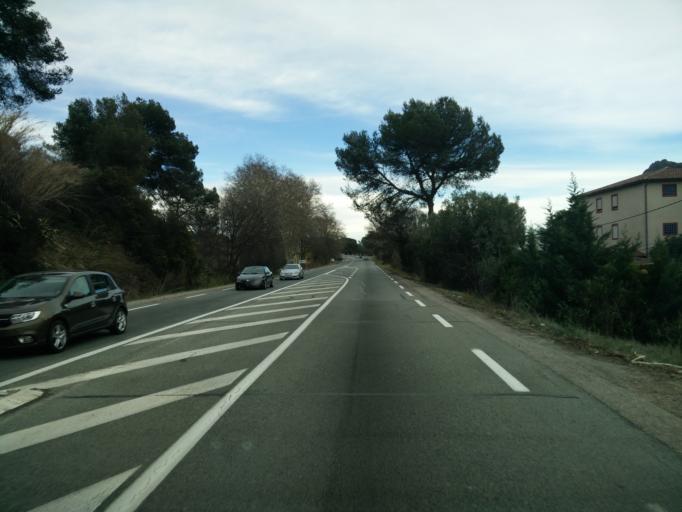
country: FR
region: Provence-Alpes-Cote d'Azur
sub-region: Departement du Var
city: Le Muy
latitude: 43.4694
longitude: 6.5830
